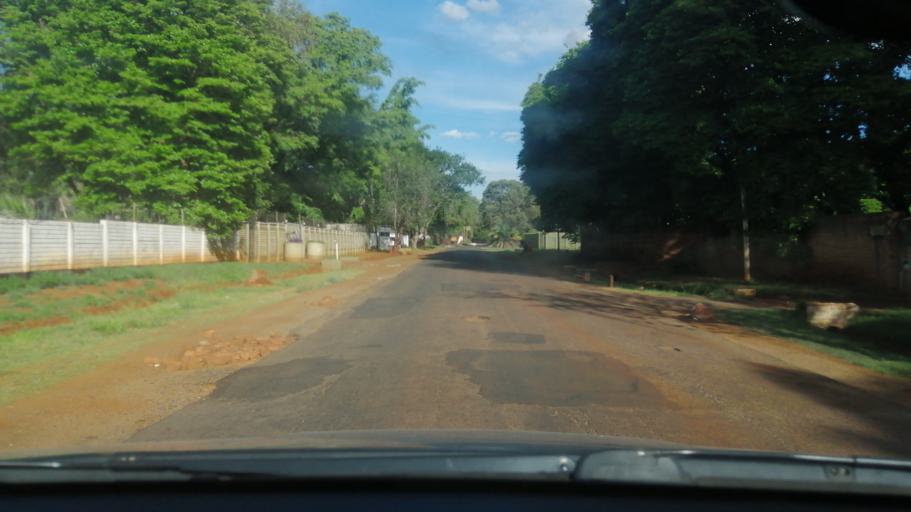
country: ZW
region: Harare
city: Harare
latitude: -17.7646
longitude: 31.0533
